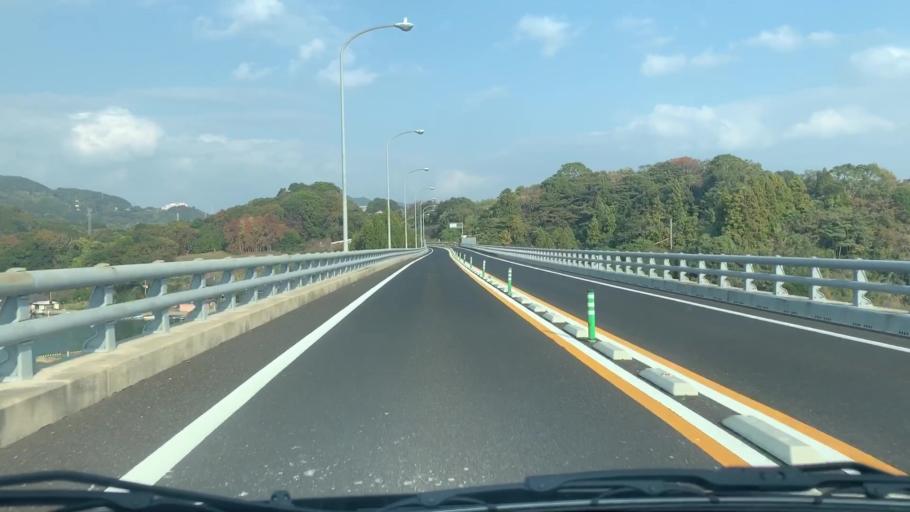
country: JP
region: Nagasaki
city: Sasebo
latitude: 33.0778
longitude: 129.7711
